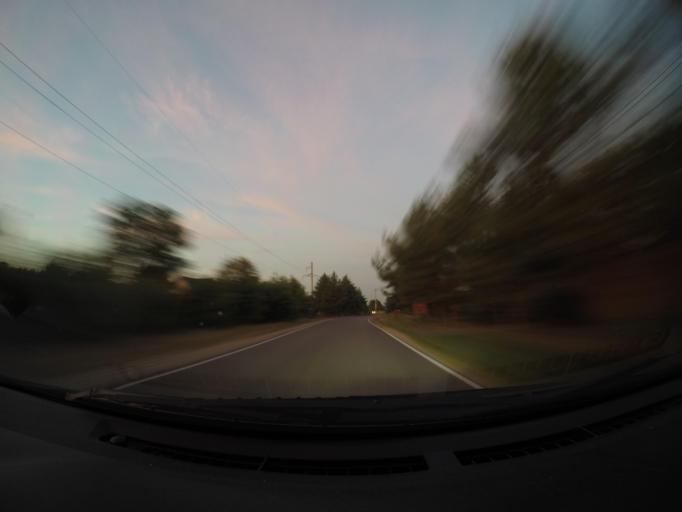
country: RU
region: Moskovskaya
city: Rechitsy
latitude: 55.5417
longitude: 38.4279
